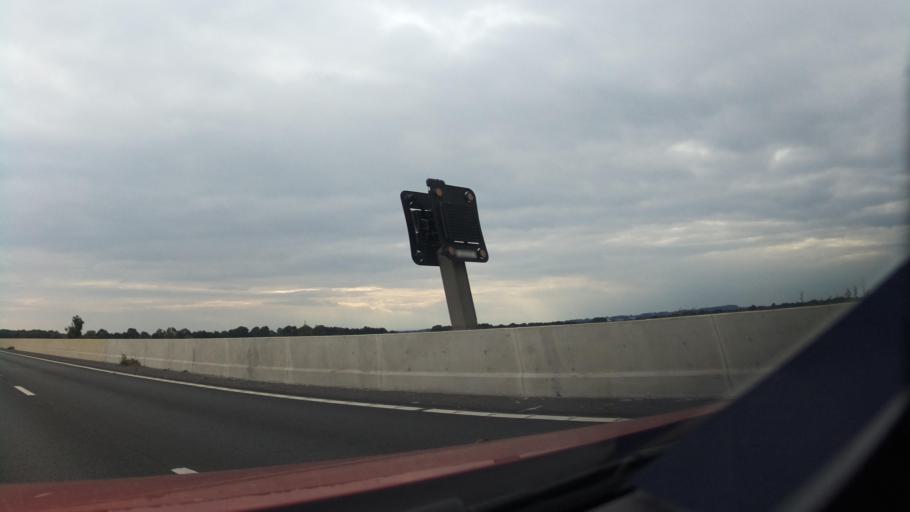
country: GB
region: England
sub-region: County Durham
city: Newton Aycliffe
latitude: 54.6149
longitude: -1.5319
